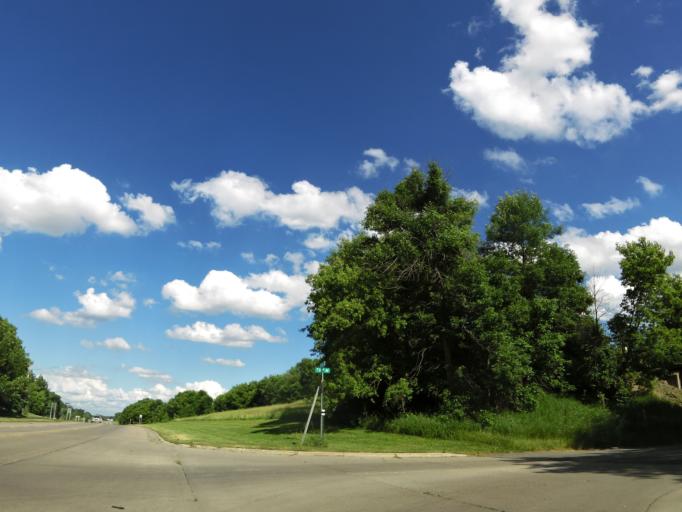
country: US
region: Minnesota
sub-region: Meeker County
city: Dassel
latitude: 45.0809
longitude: -94.2971
